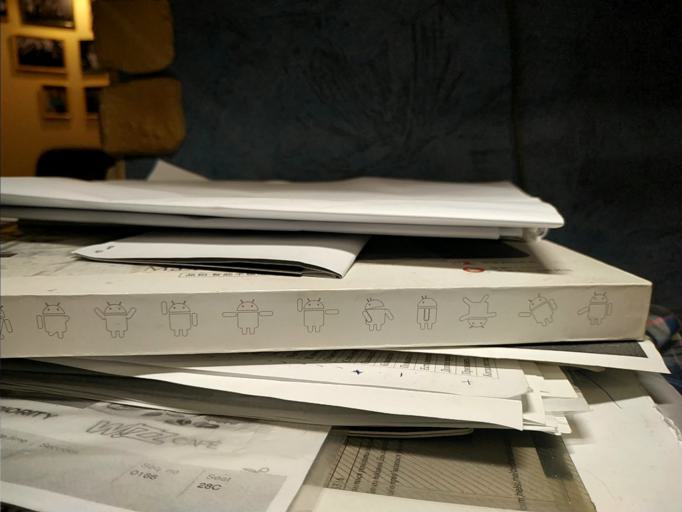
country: RU
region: Tverskaya
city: Zubtsov
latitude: 56.0847
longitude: 34.7766
